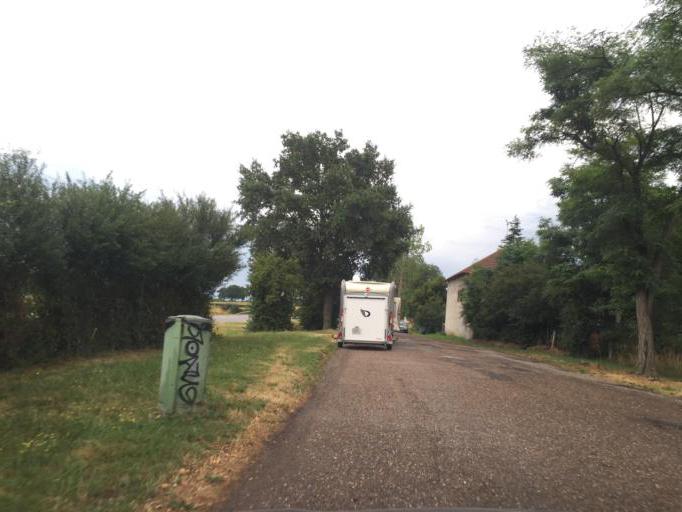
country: FR
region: Rhone-Alpes
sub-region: Departement de la Loire
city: Ambierle
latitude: 46.1297
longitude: 3.9128
